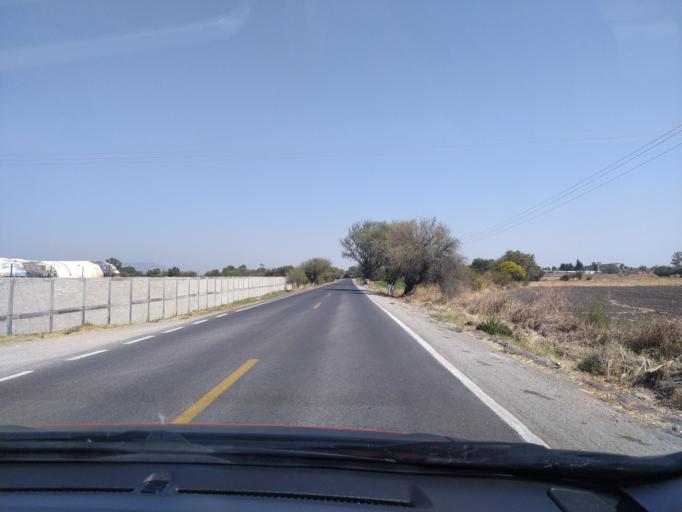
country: MX
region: Guanajuato
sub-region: San Francisco del Rincon
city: San Ignacio de Hidalgo
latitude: 20.8759
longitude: -101.8596
